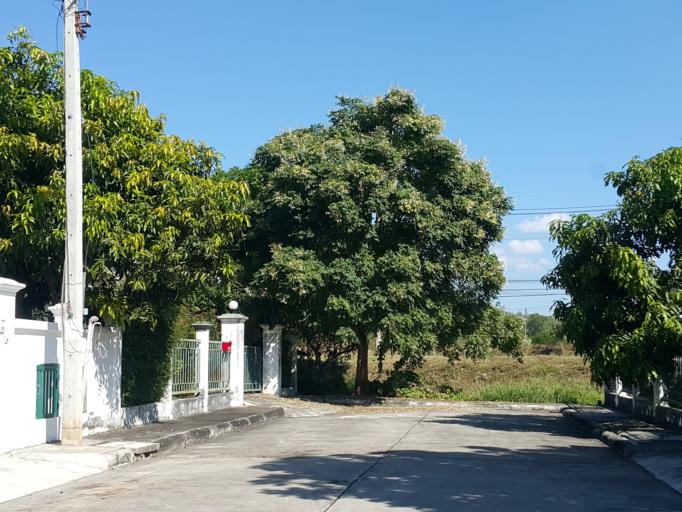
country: TH
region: Chiang Mai
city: San Sai
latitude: 18.9470
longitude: 98.9256
